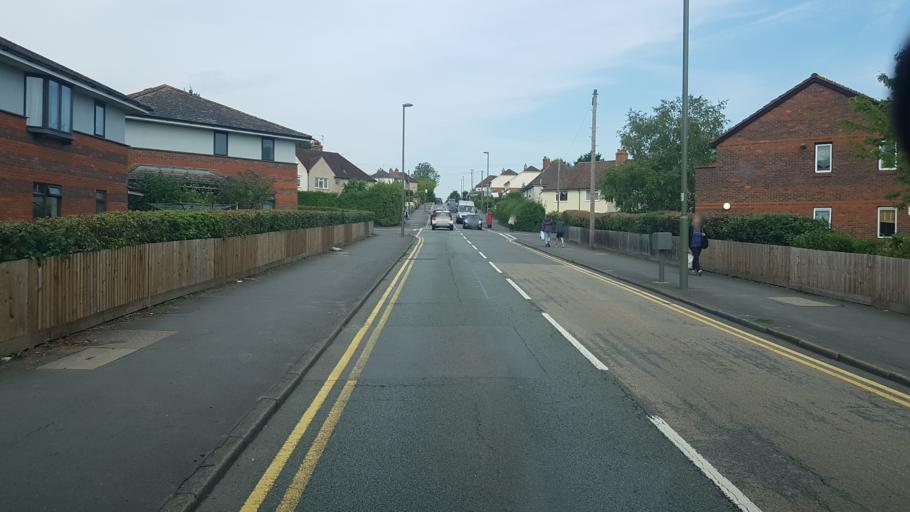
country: GB
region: England
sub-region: Surrey
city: Guildford
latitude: 51.2376
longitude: -0.5900
